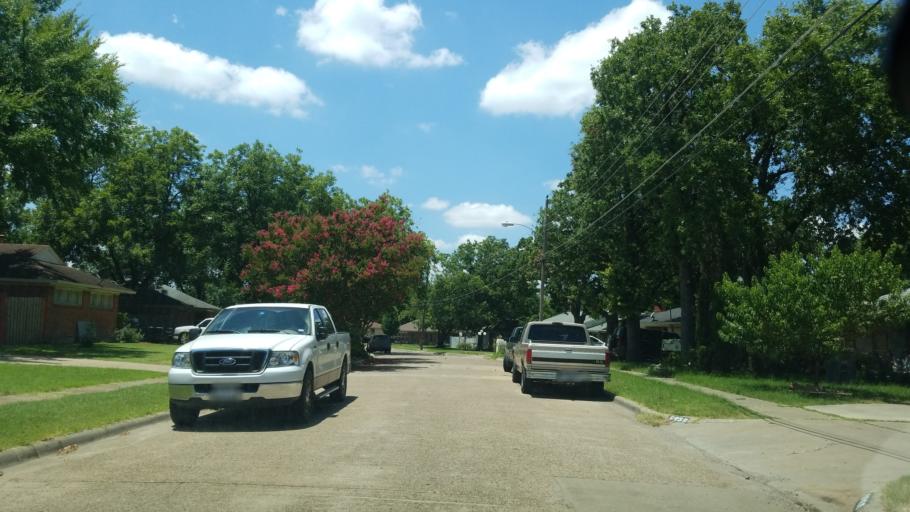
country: US
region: Texas
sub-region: Dallas County
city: Balch Springs
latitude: 32.7403
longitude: -96.7036
